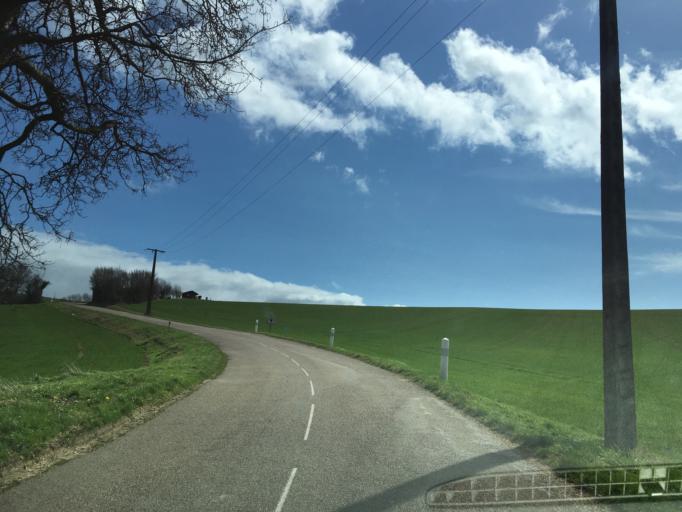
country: FR
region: Bourgogne
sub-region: Departement de l'Yonne
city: Pourrain
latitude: 47.7801
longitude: 3.4078
